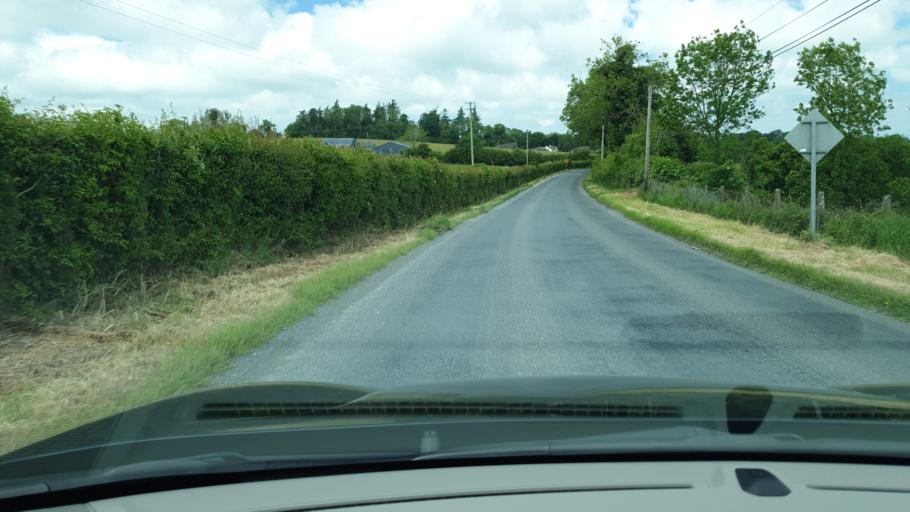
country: IE
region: Leinster
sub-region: An Mhi
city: Slane
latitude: 53.7739
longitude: -6.6296
